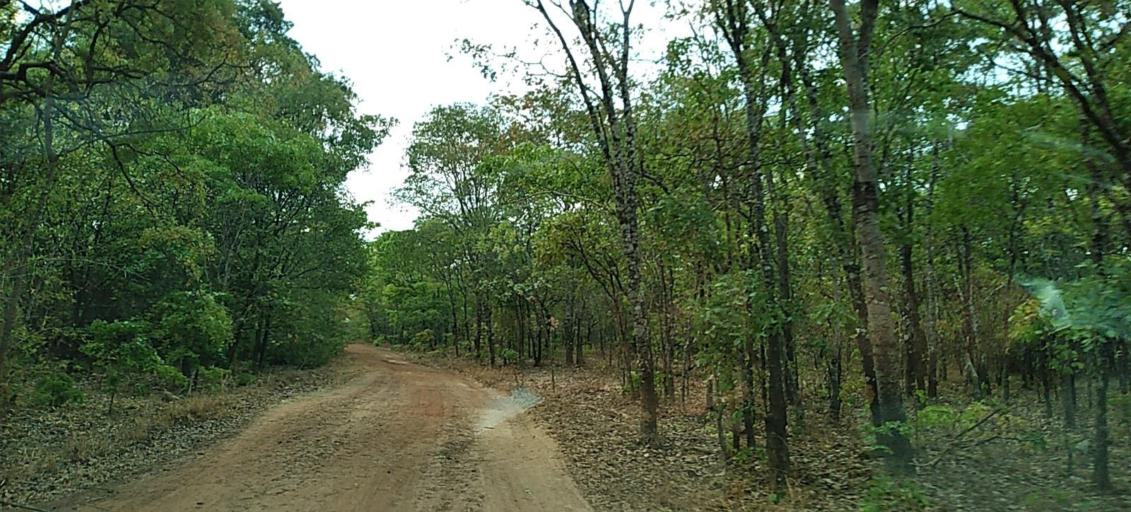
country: ZM
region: Copperbelt
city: Chililabombwe
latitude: -12.4969
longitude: 27.6405
